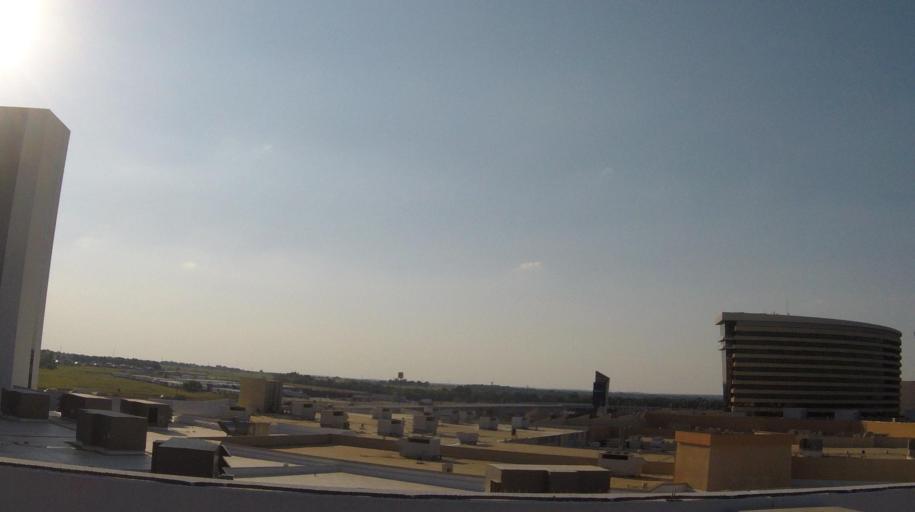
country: US
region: Oklahoma
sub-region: Bryan County
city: Calera
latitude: 33.9490
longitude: -96.4131
